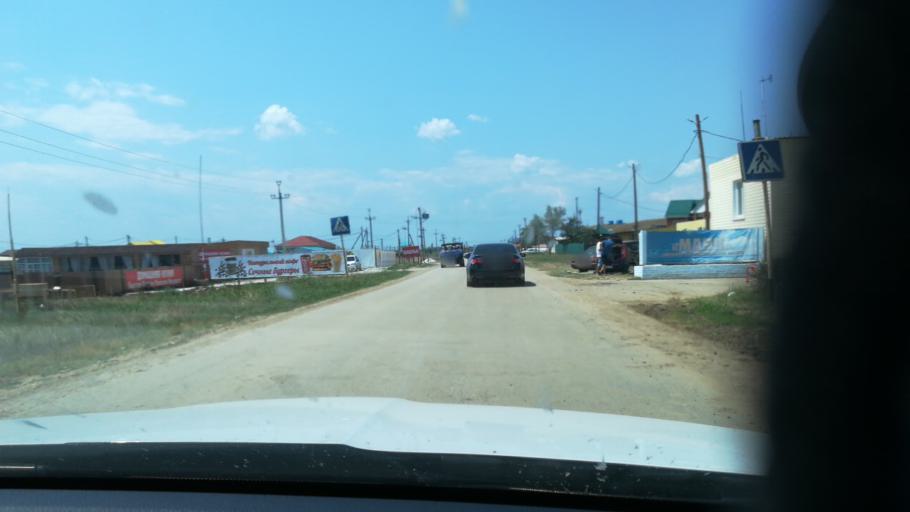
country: RU
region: Krasnodarskiy
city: Vyshestebliyevskaya
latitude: 45.1134
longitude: 36.8832
